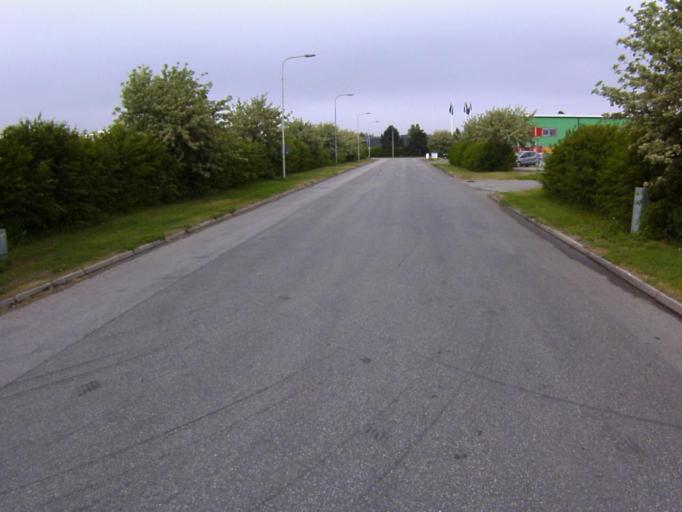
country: SE
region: Skane
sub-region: Kristianstads Kommun
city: Ahus
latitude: 55.9325
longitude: 14.2820
